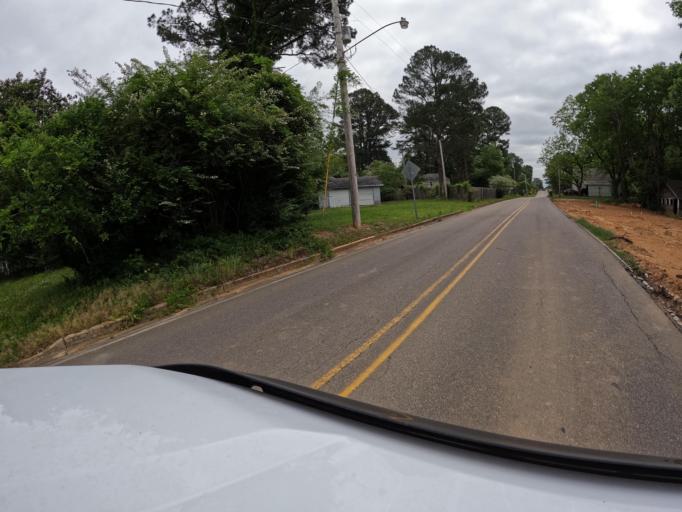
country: US
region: Mississippi
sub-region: Lee County
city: Tupelo
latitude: 34.2777
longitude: -88.7322
